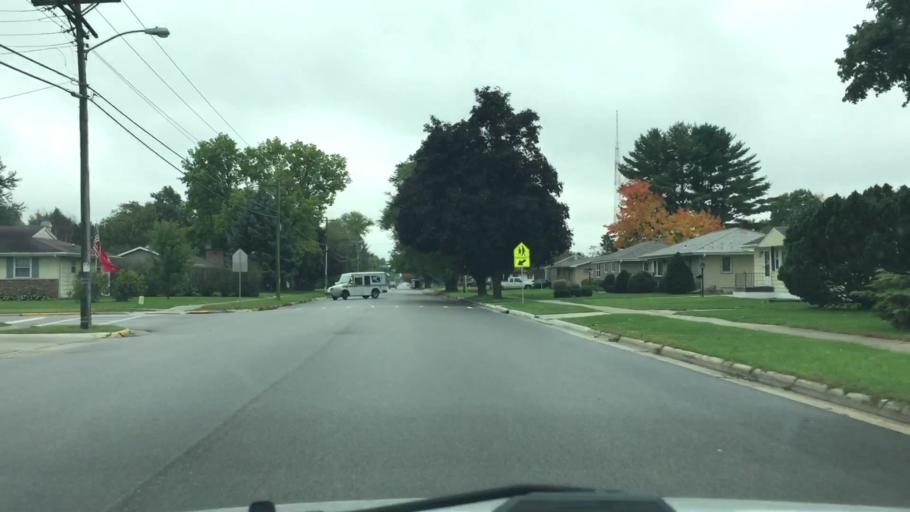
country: US
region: Wisconsin
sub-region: Rock County
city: Janesville
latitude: 42.6635
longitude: -89.0414
